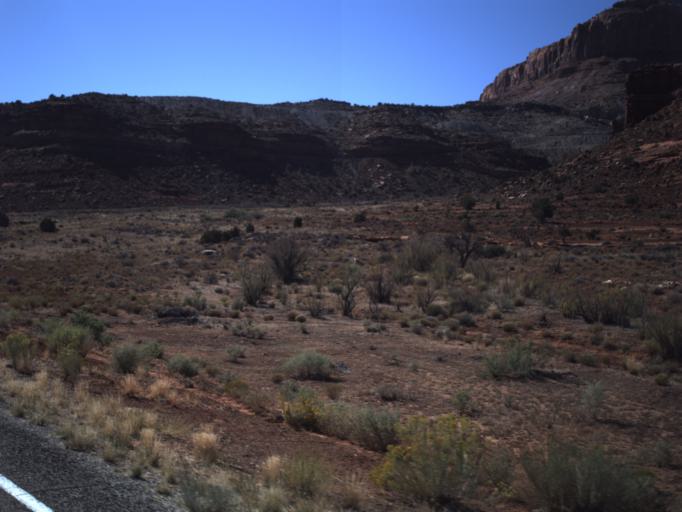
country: US
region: Utah
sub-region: San Juan County
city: Blanding
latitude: 37.7609
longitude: -110.2836
